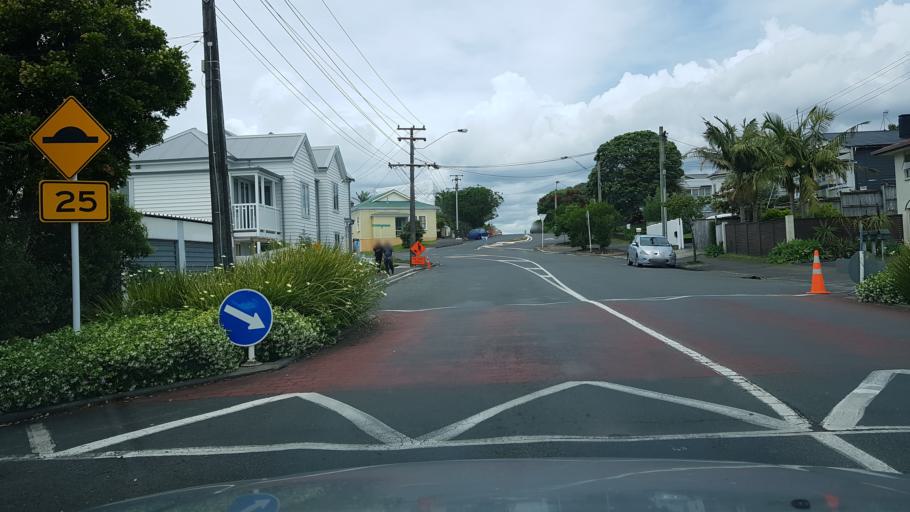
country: NZ
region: Auckland
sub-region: Auckland
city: North Shore
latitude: -36.8183
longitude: 174.7332
